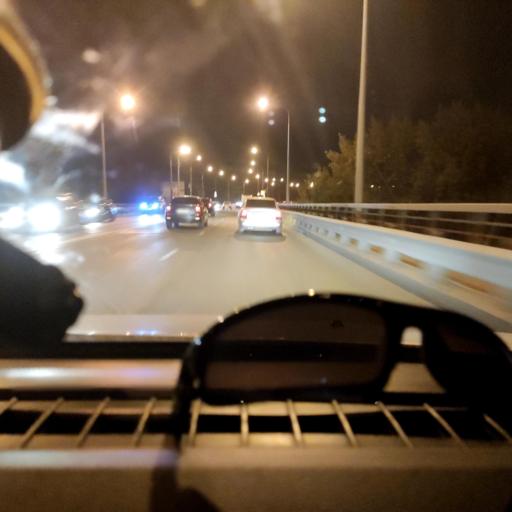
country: RU
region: Samara
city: Samara
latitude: 53.1679
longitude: 50.1962
